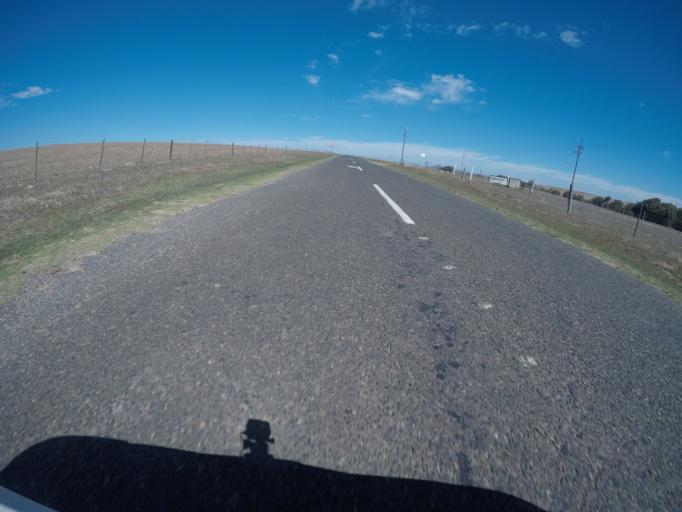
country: ZA
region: Western Cape
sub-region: City of Cape Town
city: Atlantis
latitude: -33.6193
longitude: 18.6324
